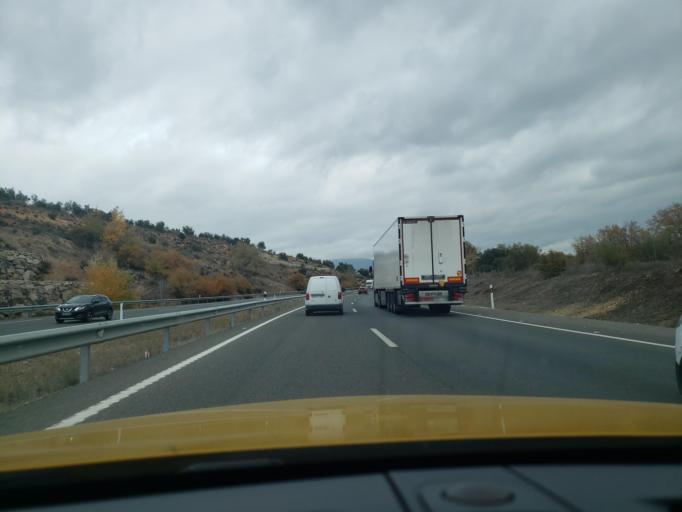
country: ES
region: Andalusia
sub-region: Provincia de Granada
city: Deifontes
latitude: 37.3307
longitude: -3.6327
